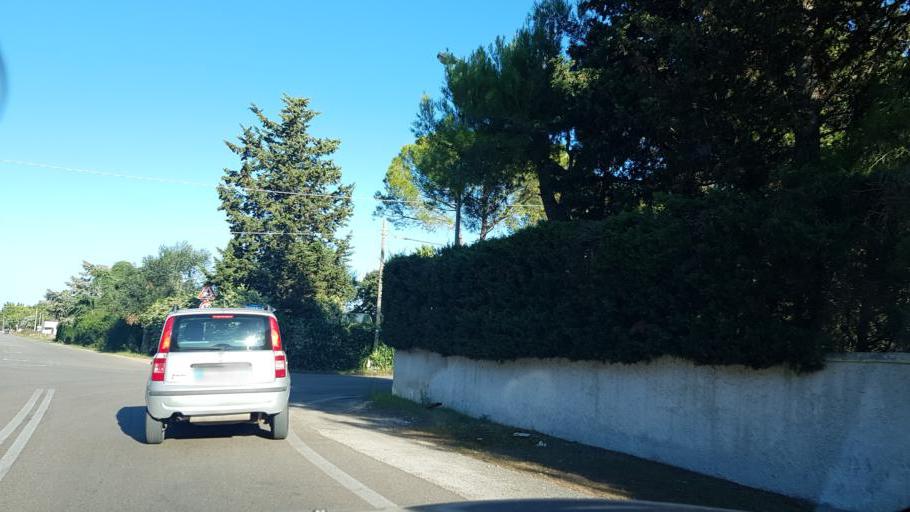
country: IT
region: Apulia
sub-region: Provincia di Lecce
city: Magliano
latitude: 40.3218
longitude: 18.0726
